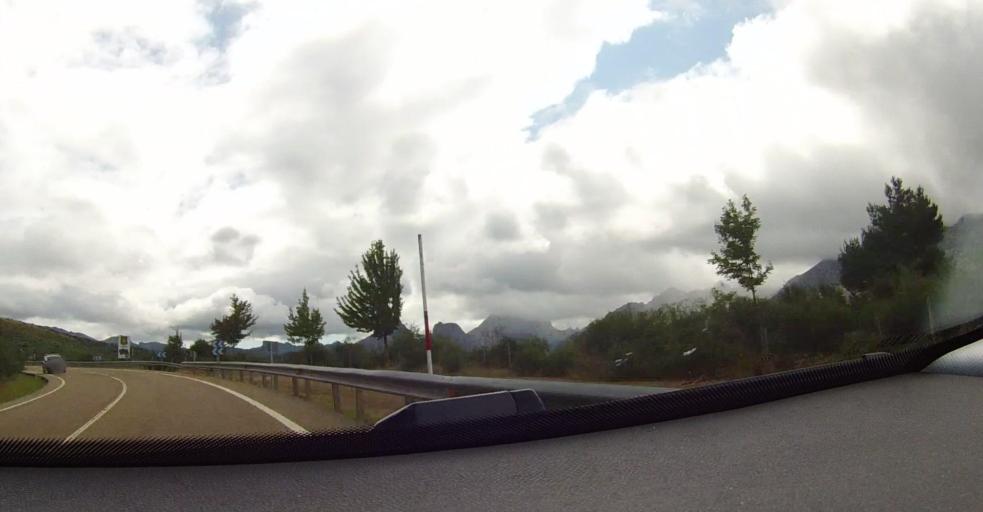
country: ES
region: Castille and Leon
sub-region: Provincia de Leon
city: Riano
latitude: 42.9851
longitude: -4.9950
